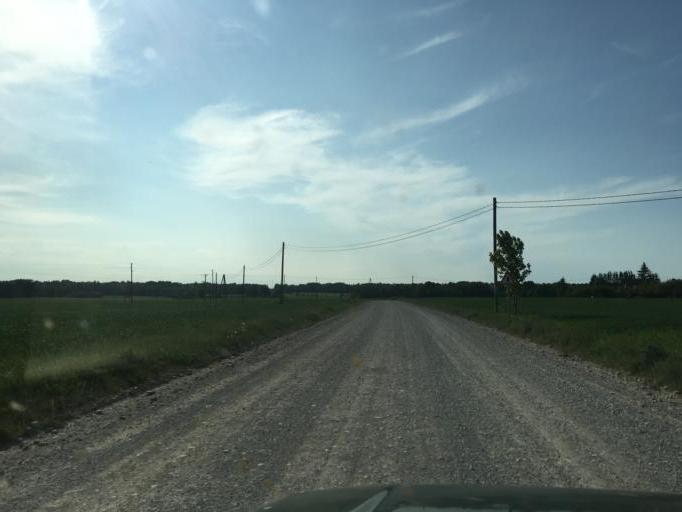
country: LV
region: Dundaga
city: Dundaga
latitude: 57.6227
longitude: 22.4076
